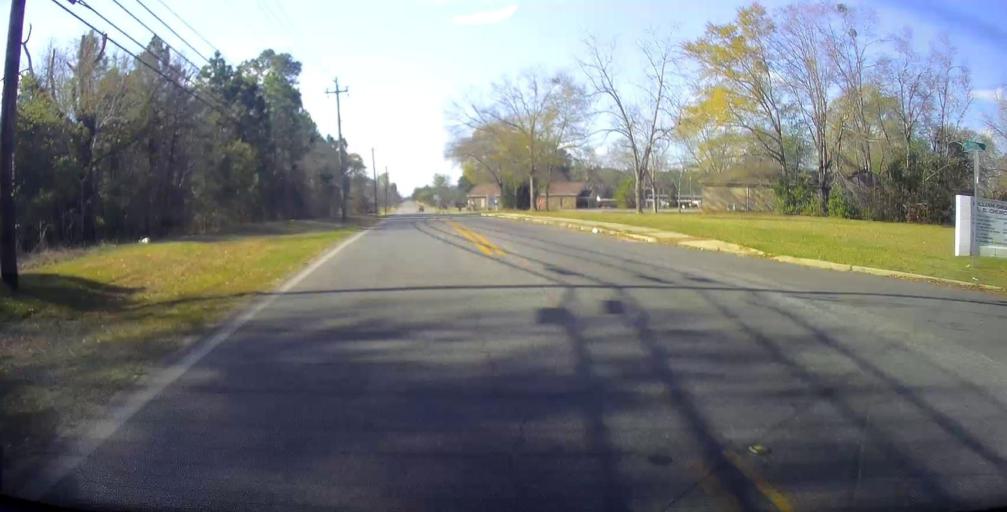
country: US
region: Georgia
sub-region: Laurens County
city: Dublin
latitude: 32.5429
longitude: -82.9186
